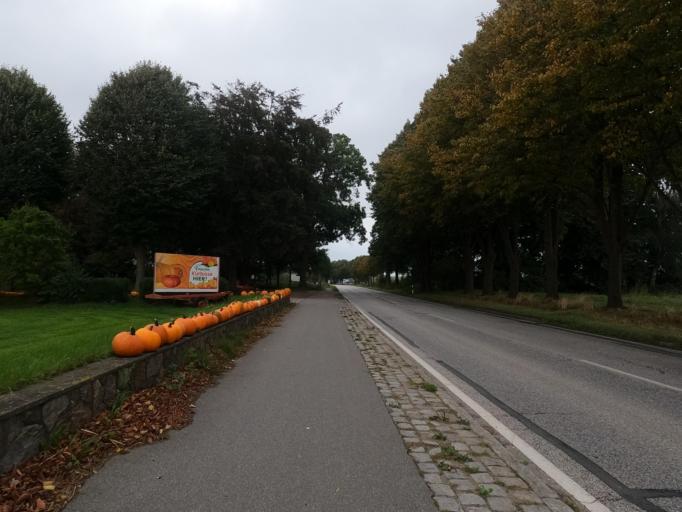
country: DE
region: Schleswig-Holstein
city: Heiligenhafen
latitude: 54.3554
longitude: 11.0109
